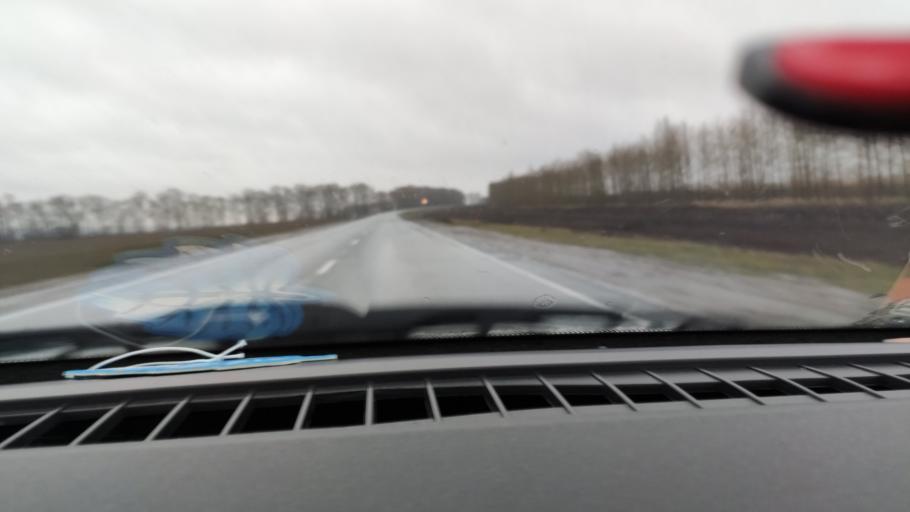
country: RU
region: Tatarstan
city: Mendeleyevsk
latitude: 55.8499
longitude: 52.2097
